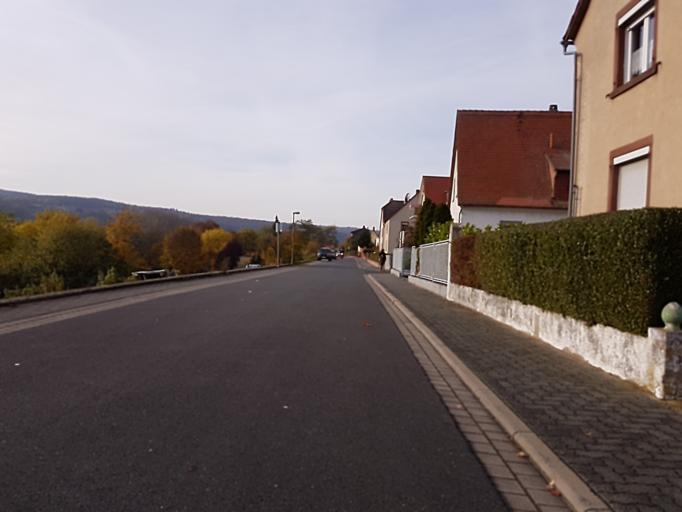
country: DE
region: Bavaria
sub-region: Regierungsbezirk Unterfranken
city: Worth am Main
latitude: 49.8011
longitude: 9.1569
